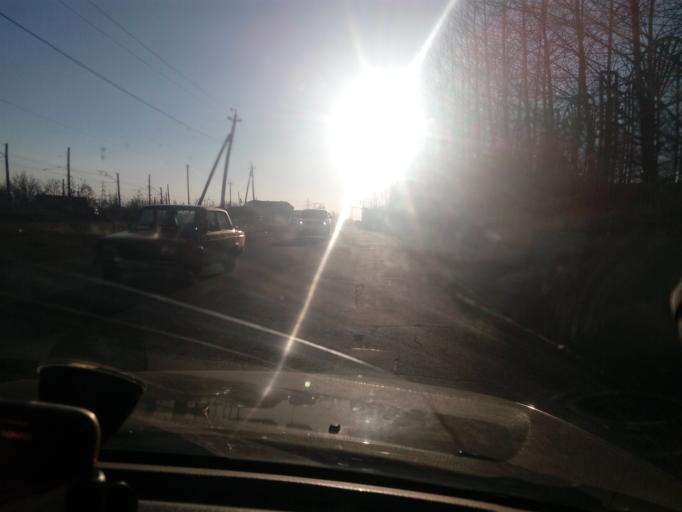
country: AM
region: Kotayk'i Marz
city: Balahovit
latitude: 40.2533
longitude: 44.5961
